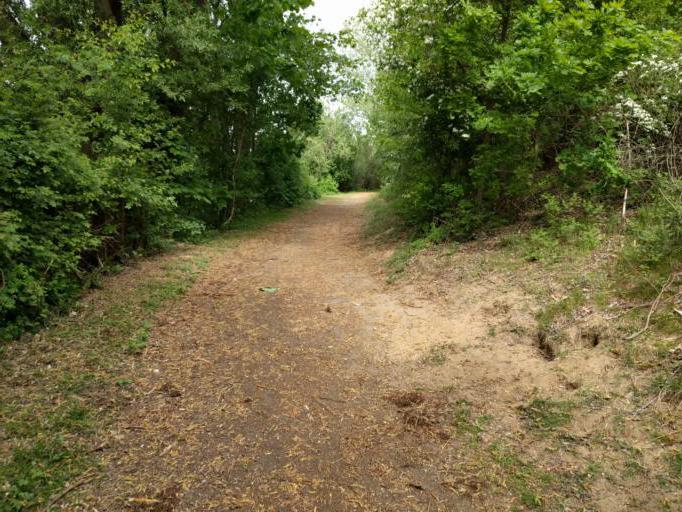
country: DE
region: Lower Saxony
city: Peine
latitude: 52.3482
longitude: 10.2019
